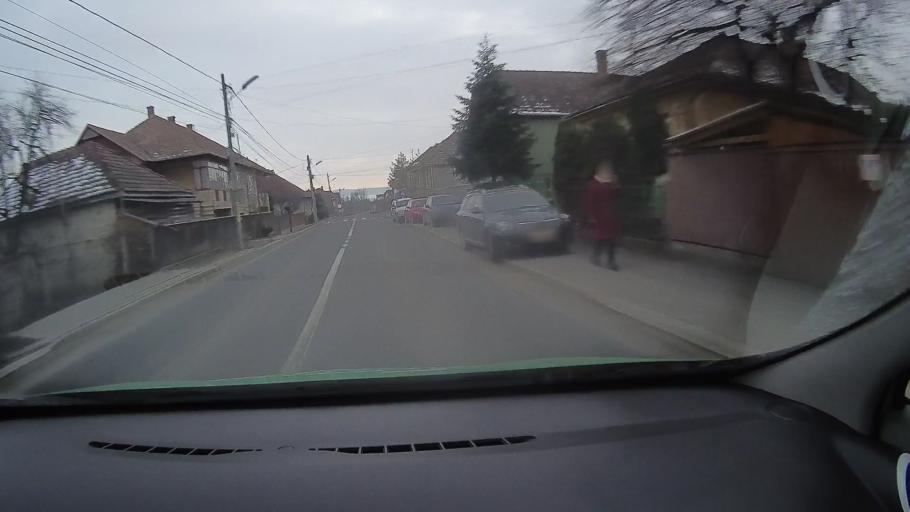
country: RO
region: Harghita
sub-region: Municipiul Odorheiu Secuiesc
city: Odorheiu Secuiesc
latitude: 46.3089
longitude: 25.2860
